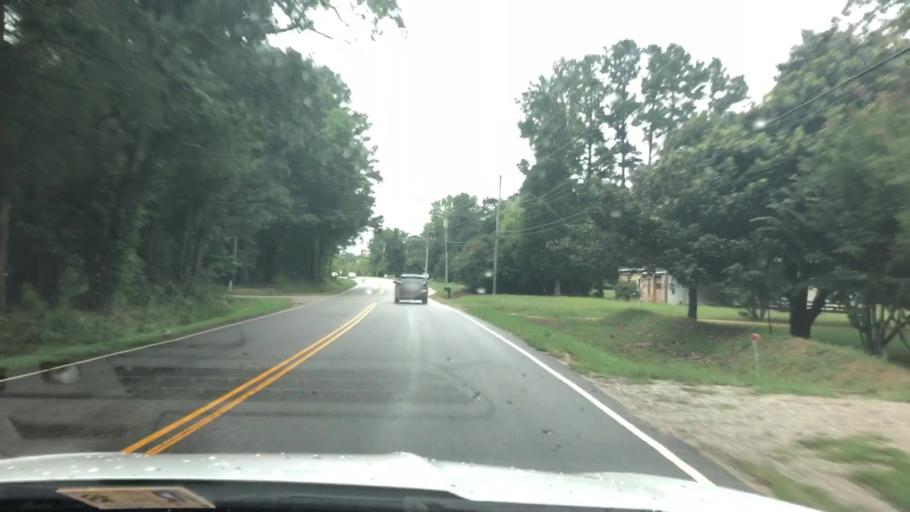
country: US
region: Virginia
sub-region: James City County
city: Williamsburg
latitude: 37.2572
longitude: -76.7653
